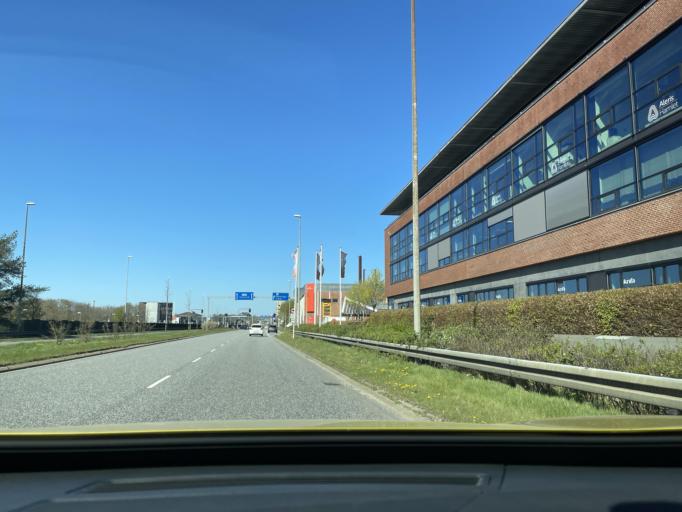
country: DK
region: Central Jutland
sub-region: Herning Kommune
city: Herning
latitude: 56.1319
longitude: 8.9859
